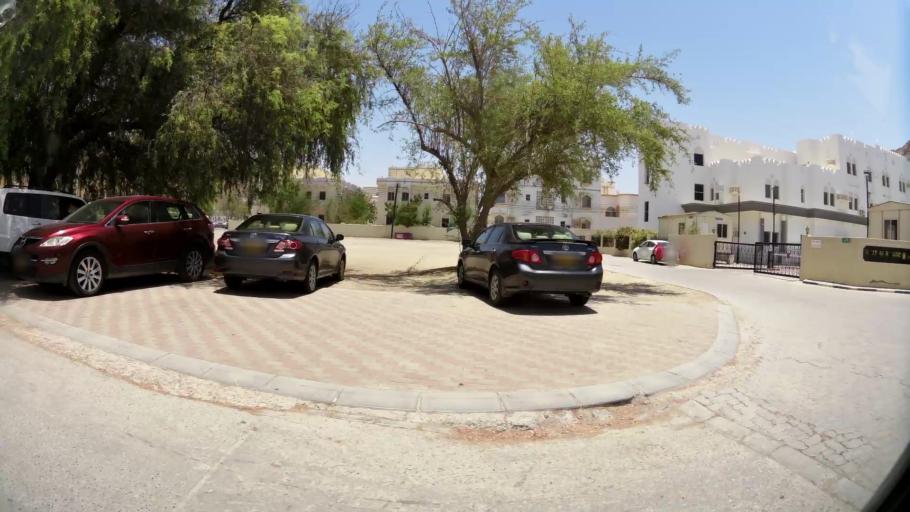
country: OM
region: Muhafazat Masqat
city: Muscat
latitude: 23.6264
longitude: 58.5399
